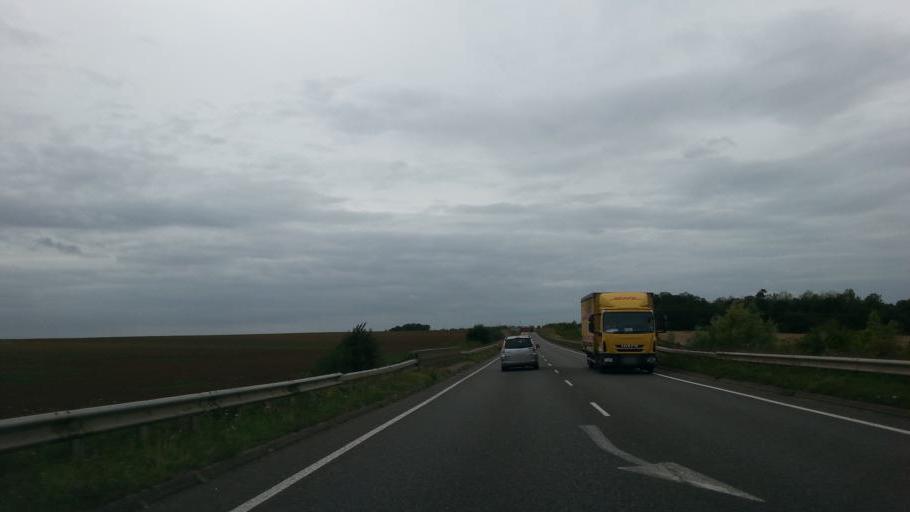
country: GB
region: England
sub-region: Cambridgeshire
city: Papworth Everard
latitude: 52.2414
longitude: -0.1188
